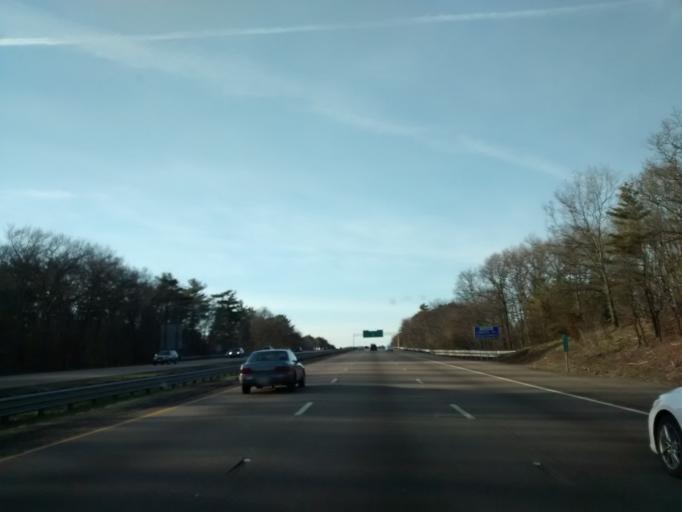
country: US
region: Massachusetts
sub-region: Norfolk County
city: Randolph
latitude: 42.1809
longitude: -71.0757
